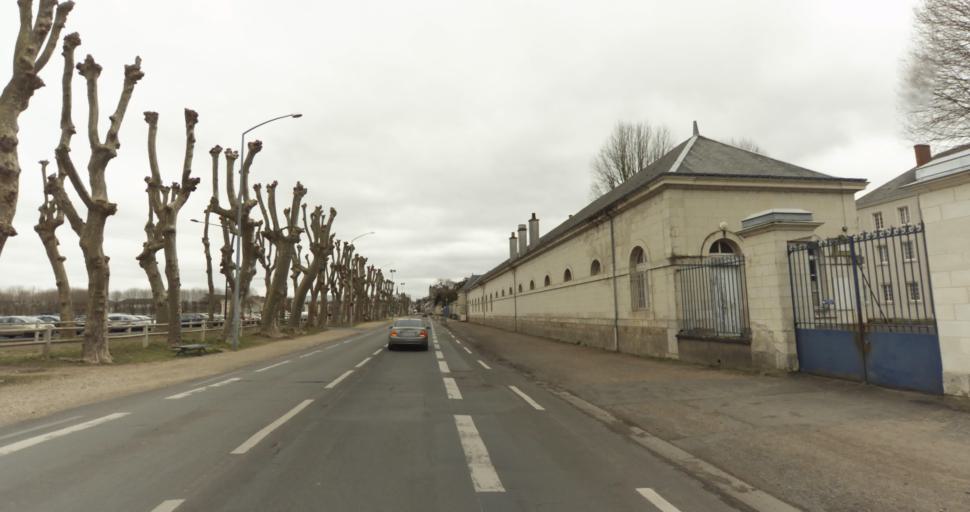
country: FR
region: Pays de la Loire
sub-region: Departement de Maine-et-Loire
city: Saumur
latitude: 47.2622
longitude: -0.0873
